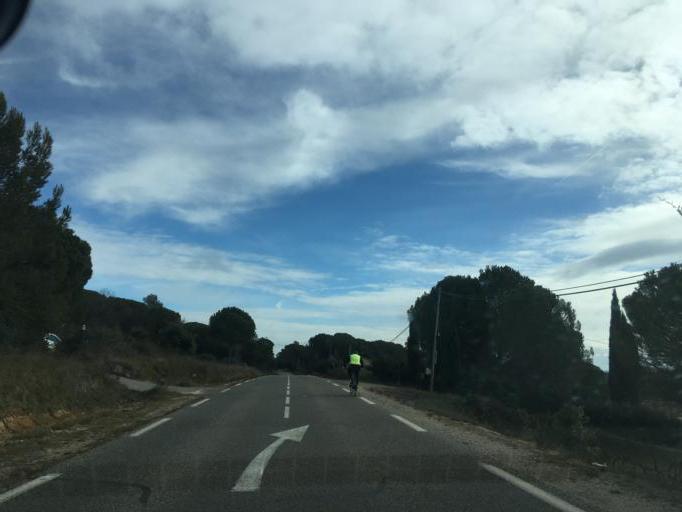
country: FR
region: Provence-Alpes-Cote d'Azur
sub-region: Departement du Var
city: Le Val
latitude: 43.4440
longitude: 6.0220
